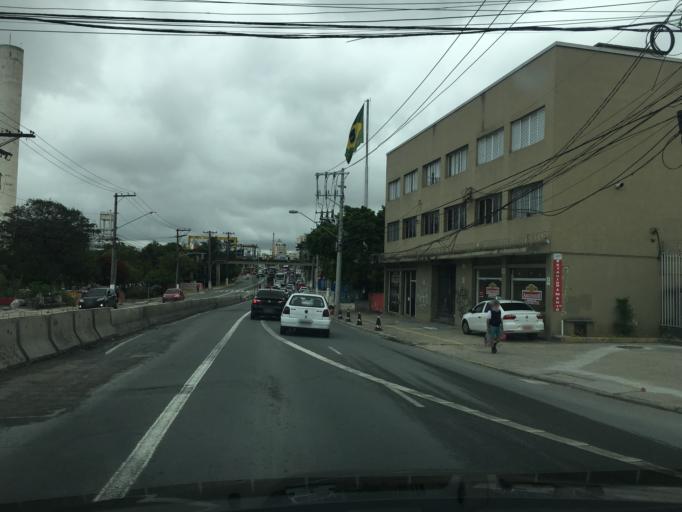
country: BR
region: Sao Paulo
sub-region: Taboao Da Serra
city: Taboao da Serra
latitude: -23.5952
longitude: -46.7389
